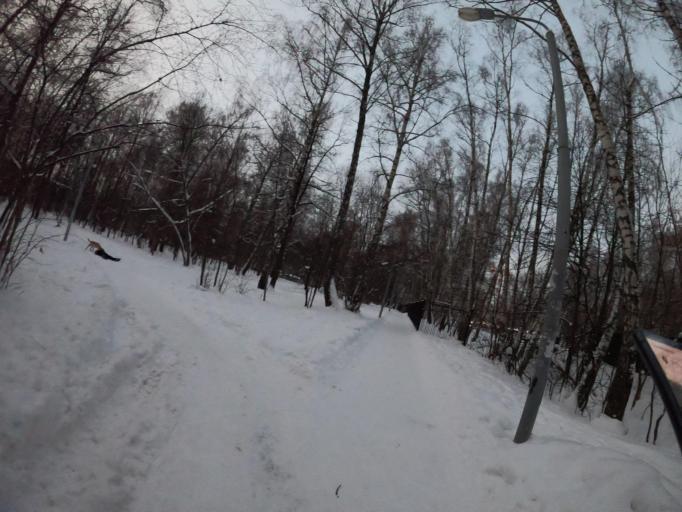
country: RU
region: Moskovskaya
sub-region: Podol'skiy Rayon
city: Podol'sk
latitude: 55.4167
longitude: 37.5257
